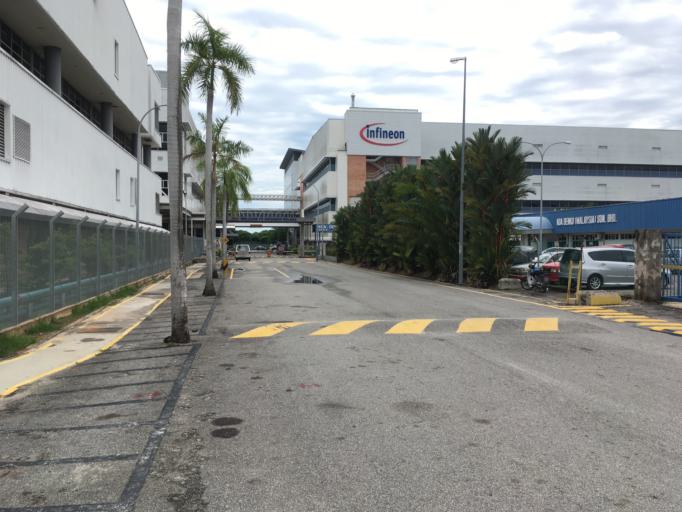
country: MY
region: Melaka
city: Batu Berendam
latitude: 2.2336
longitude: 102.2599
